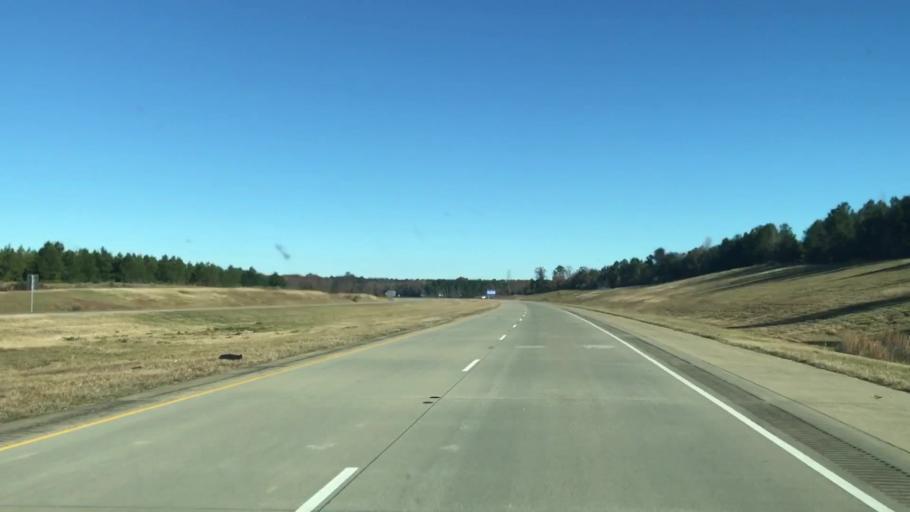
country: US
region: Louisiana
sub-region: Caddo Parish
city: Vivian
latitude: 33.0146
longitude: -93.9021
